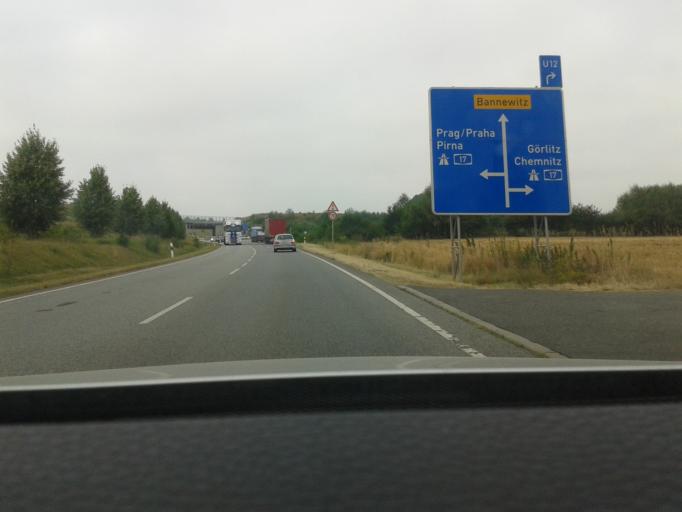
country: DE
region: Saxony
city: Kreischa
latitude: 50.9951
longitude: 13.7714
